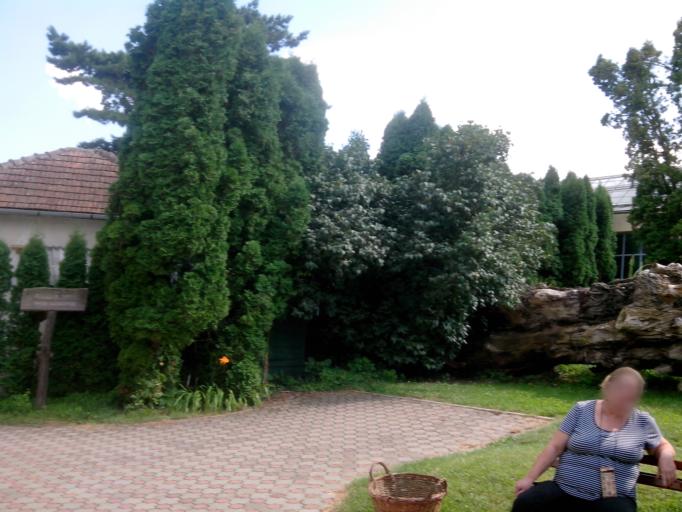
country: RO
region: Cluj
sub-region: Municipiul Cluj-Napoca
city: Cluj-Napoca
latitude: 46.7603
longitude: 23.5888
